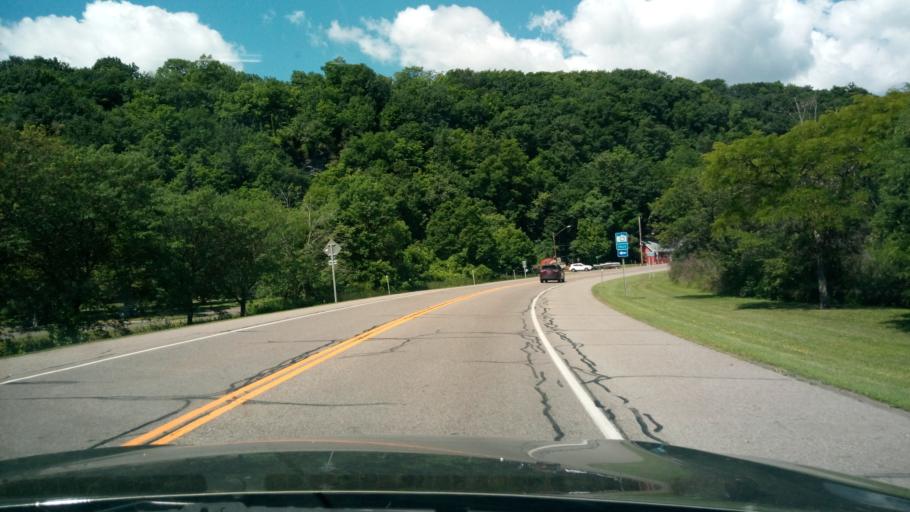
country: US
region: New York
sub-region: Schuyler County
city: Montour Falls
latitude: 42.3507
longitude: -76.8528
